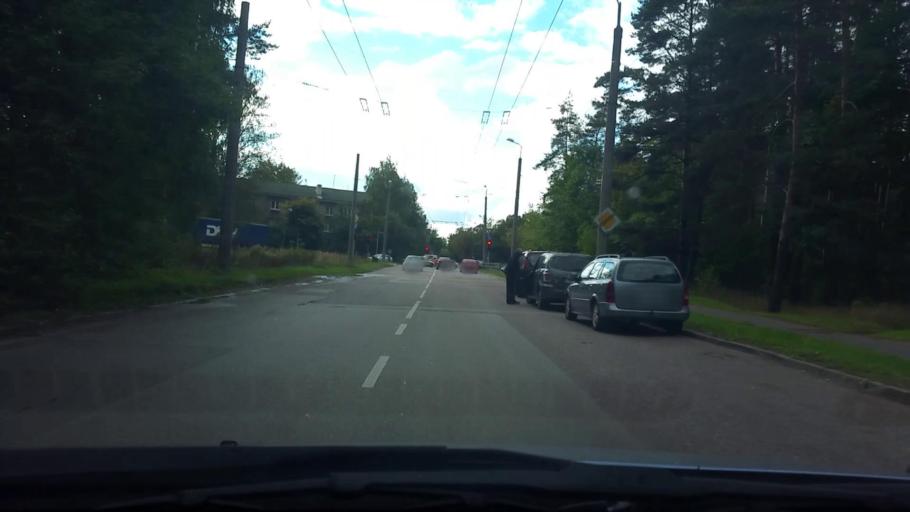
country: LV
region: Riga
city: Jaunciems
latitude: 56.9672
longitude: 24.1984
